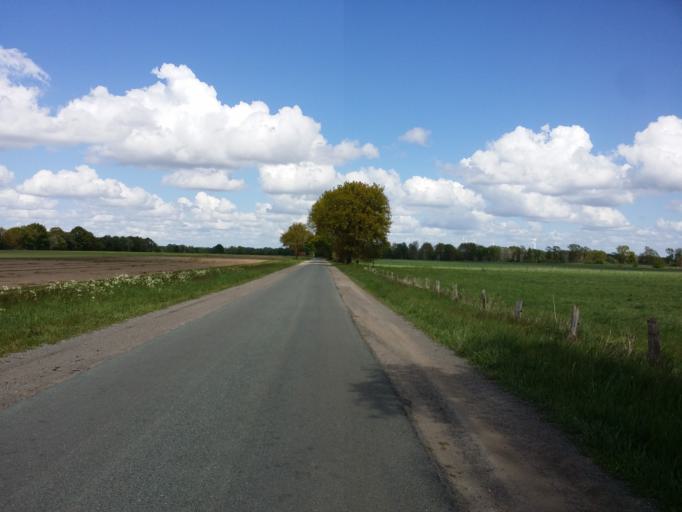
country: DE
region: Lower Saxony
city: Gross Ippener
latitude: 52.9798
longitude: 8.5975
